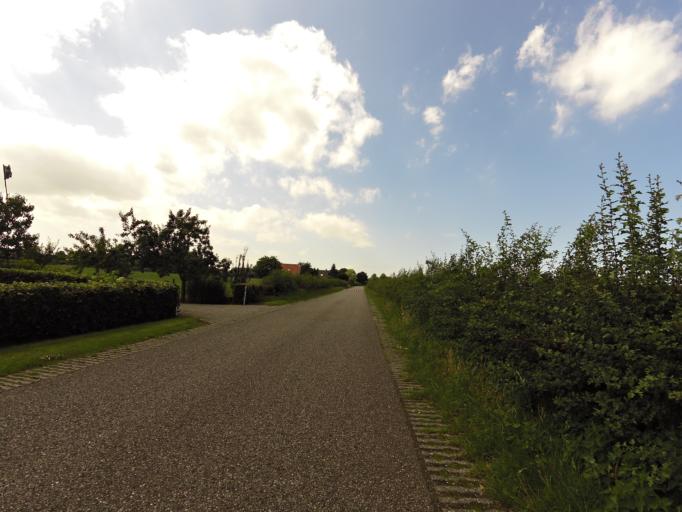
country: NL
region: Gelderland
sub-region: Gemeente Doesburg
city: Doesburg
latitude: 51.9609
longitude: 6.1724
